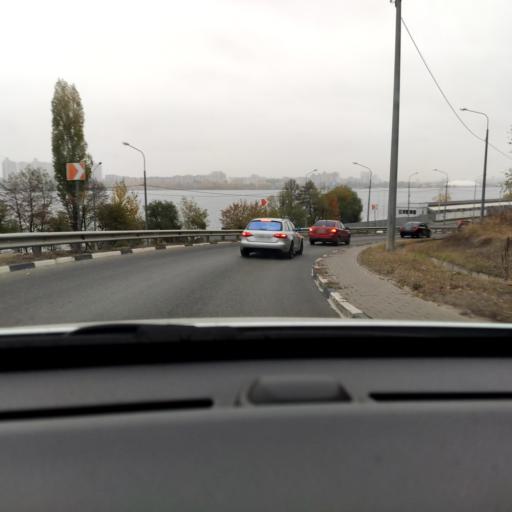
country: RU
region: Voronezj
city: Voronezh
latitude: 51.6933
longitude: 39.2328
